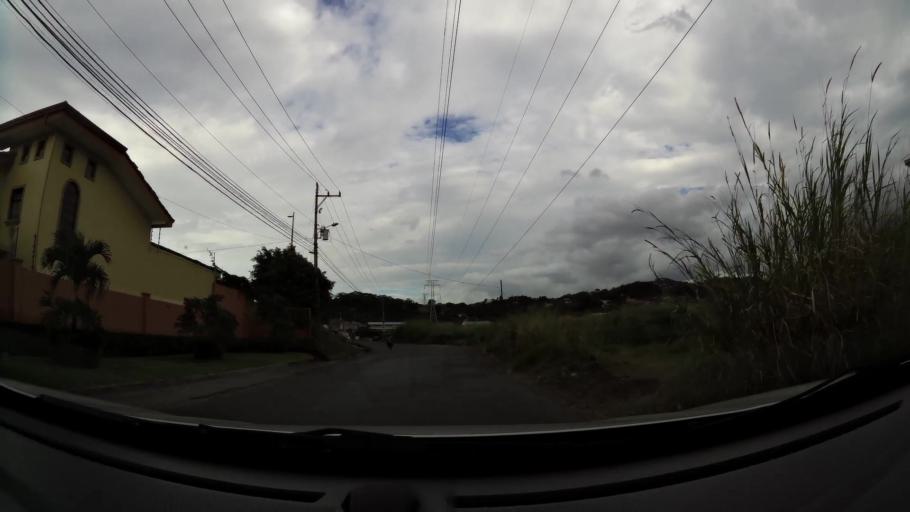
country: CR
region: Heredia
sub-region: Canton de Belen
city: San Antonio
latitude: 9.9660
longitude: -84.1927
